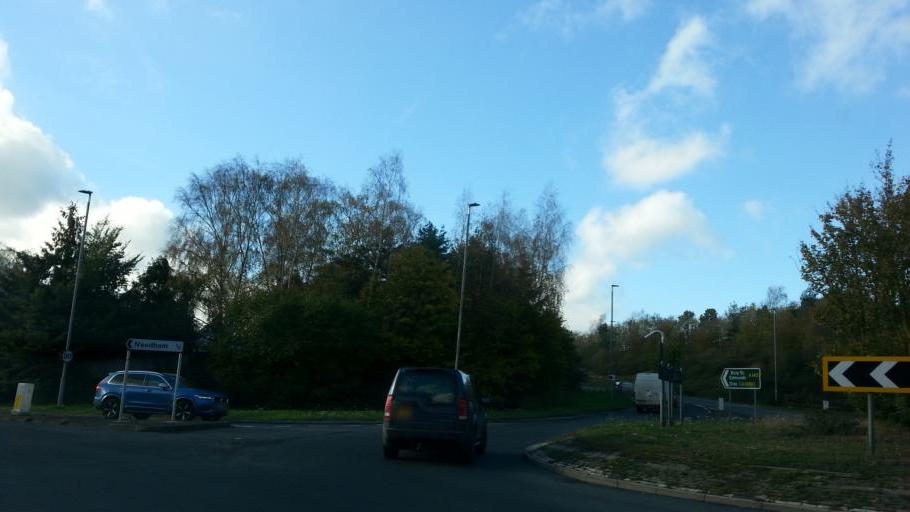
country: GB
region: England
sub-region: Norfolk
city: Harleston
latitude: 52.3925
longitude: 1.2842
